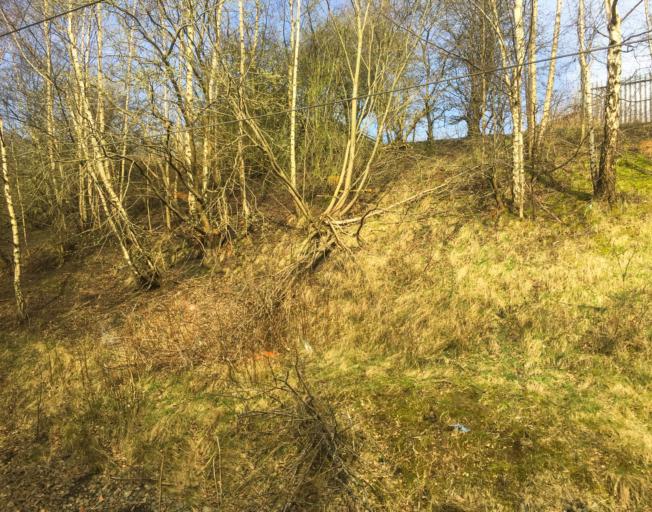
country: GB
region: Scotland
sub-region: North Lanarkshire
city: Coatbridge
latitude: 55.8498
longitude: -4.0120
